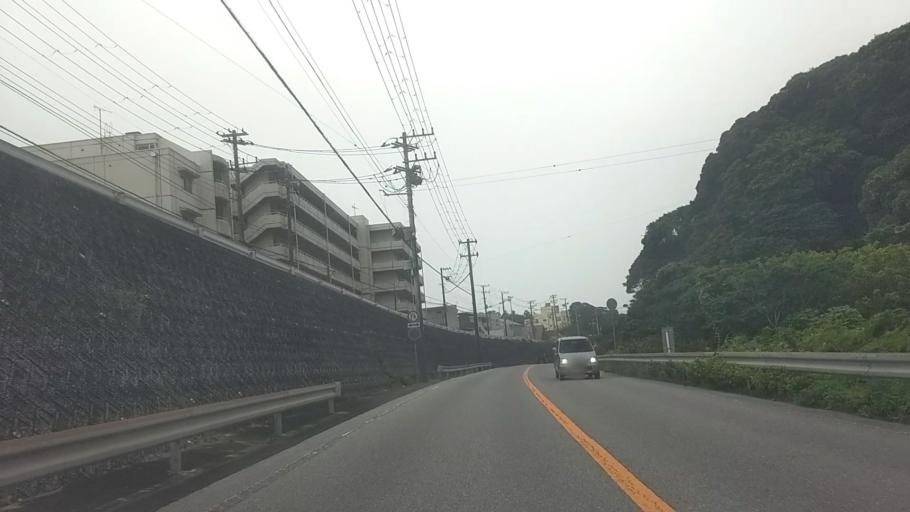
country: JP
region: Chiba
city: Katsuura
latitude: 35.1601
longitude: 140.3180
